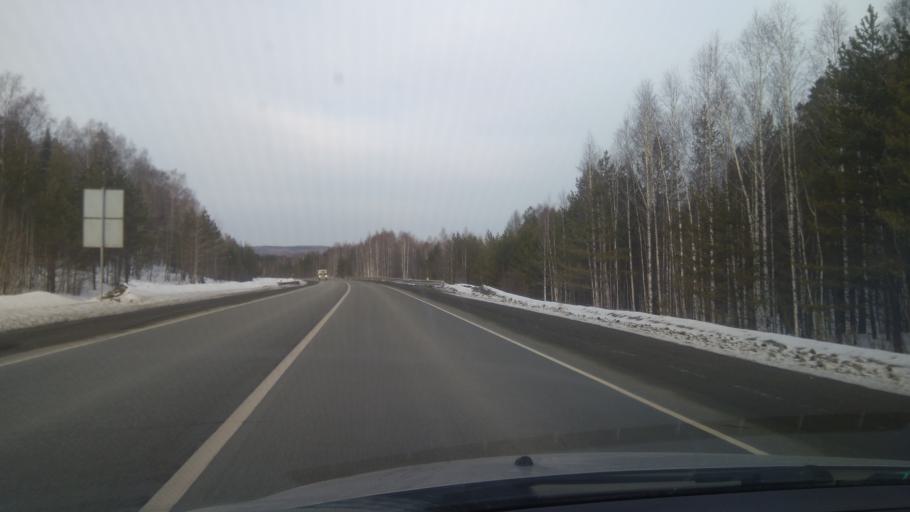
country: RU
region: Sverdlovsk
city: Bisert'
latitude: 56.8369
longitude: 58.8782
